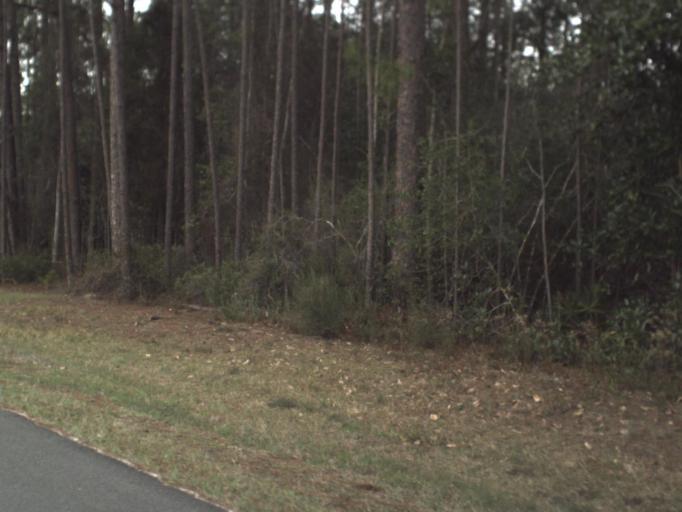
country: US
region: Florida
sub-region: Gulf County
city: Wewahitchka
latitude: 30.1357
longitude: -85.2408
